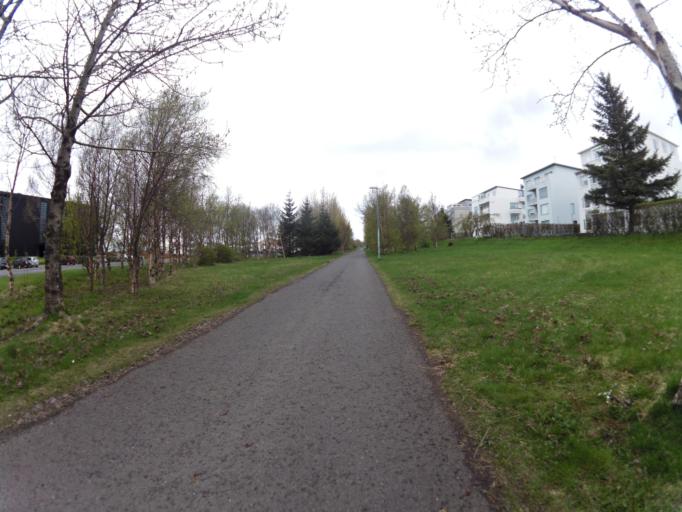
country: IS
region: Capital Region
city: Reykjavik
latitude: 64.1285
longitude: -21.8571
